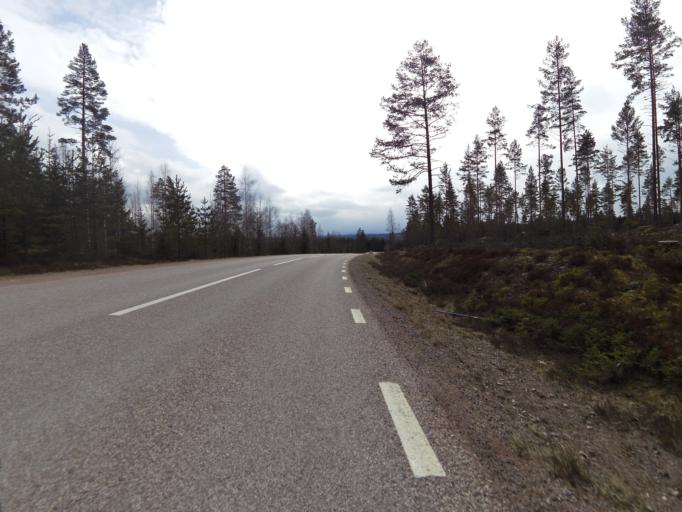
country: SE
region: Dalarna
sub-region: Hedemora Kommun
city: Langshyttan
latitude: 60.5239
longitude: 16.1356
